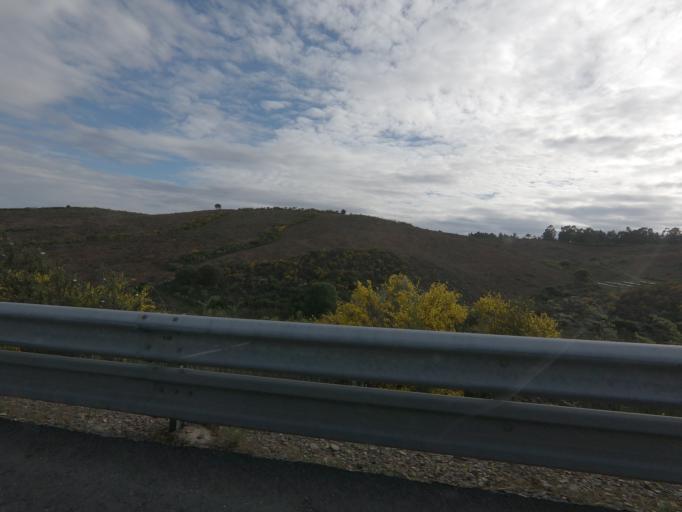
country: ES
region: Extremadura
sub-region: Provincia de Caceres
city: Perales del Puerto
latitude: 40.1256
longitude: -6.6793
